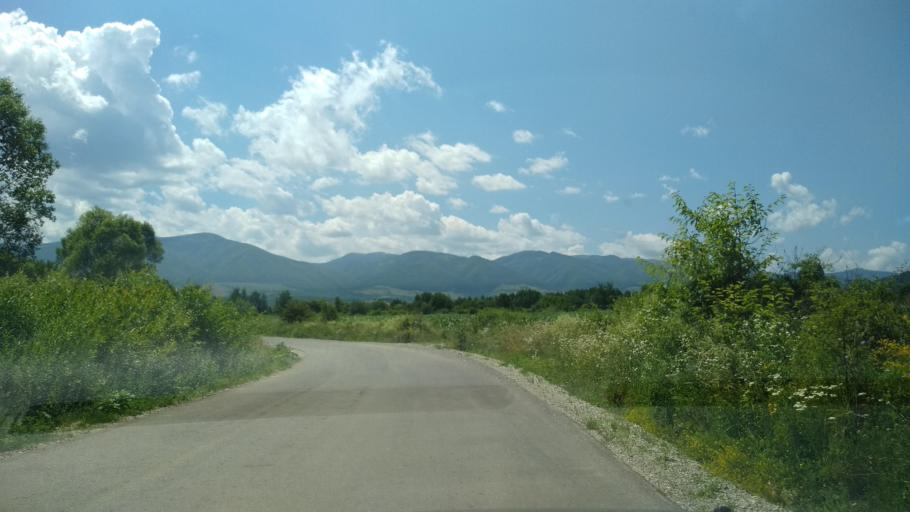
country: RO
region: Hunedoara
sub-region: Comuna Sarmizegetusa
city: Sarmizegetusa
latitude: 45.5356
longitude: 22.8186
